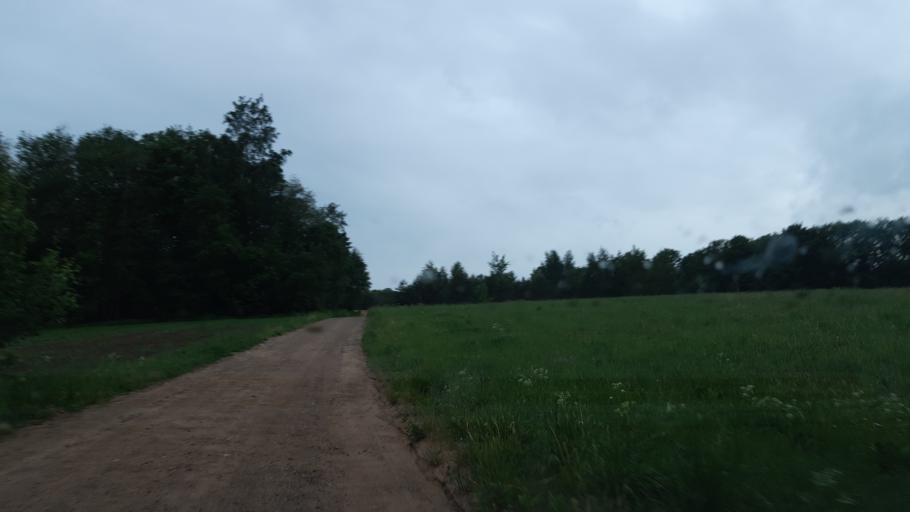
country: LT
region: Utenos apskritis
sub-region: Anyksciai
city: Anyksciai
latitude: 55.4529
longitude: 25.2146
